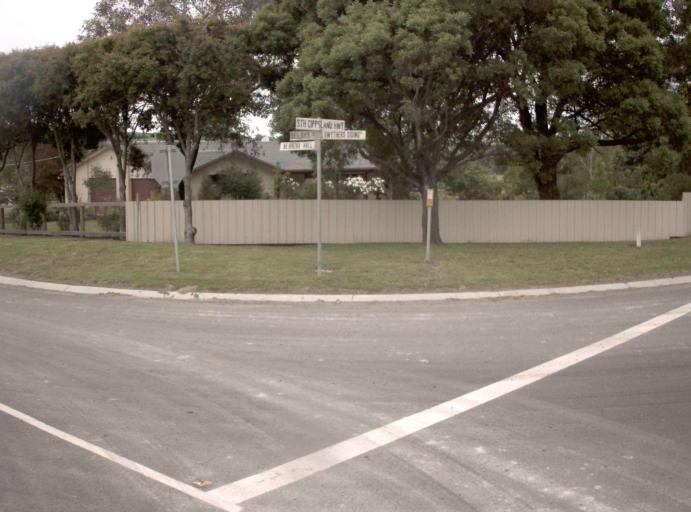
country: AU
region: Victoria
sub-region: Baw Baw
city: Warragul
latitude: -38.5185
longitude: 145.9519
